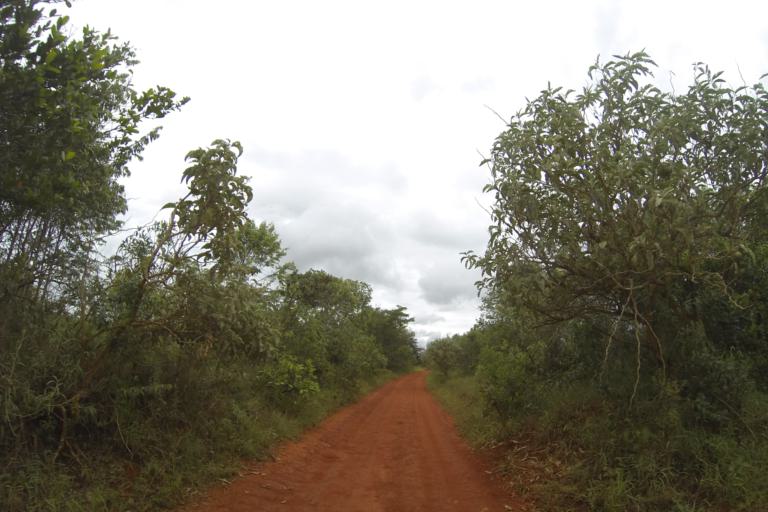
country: BR
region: Minas Gerais
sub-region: Ibia
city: Ibia
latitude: -19.7365
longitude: -46.5685
